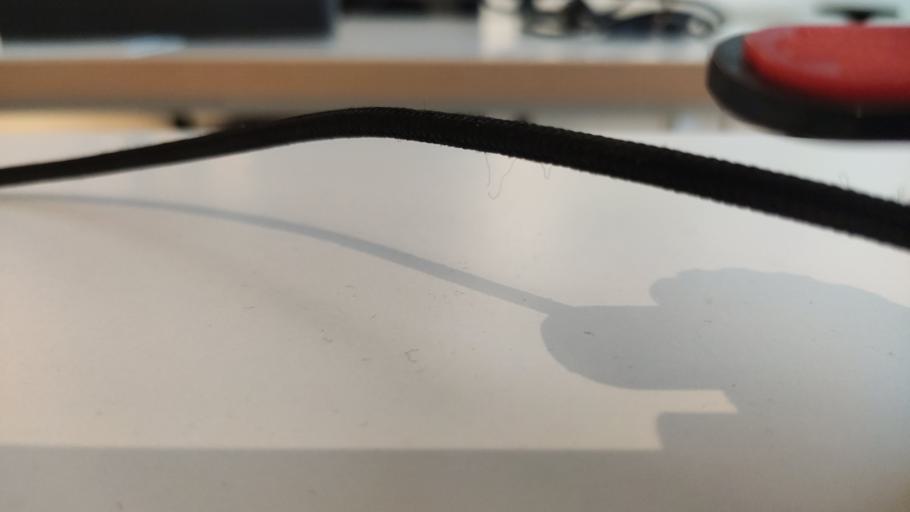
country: RU
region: Moskovskaya
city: Novopetrovskoye
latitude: 55.9661
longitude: 36.4406
